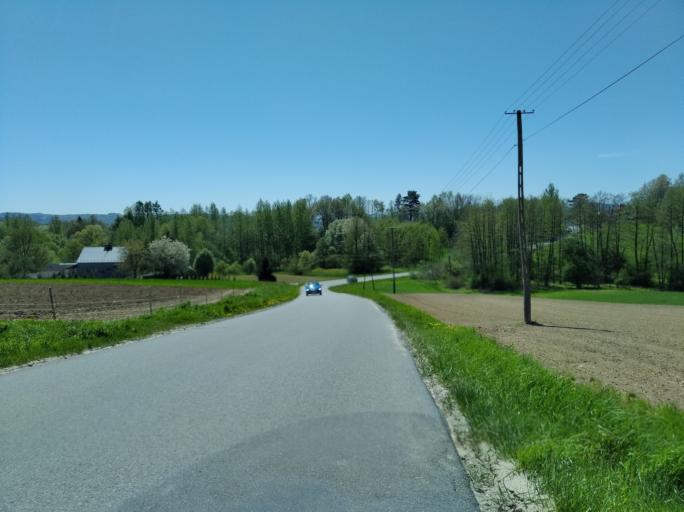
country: PL
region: Subcarpathian Voivodeship
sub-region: Powiat debicki
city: Brzostek
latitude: 49.8976
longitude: 21.4081
